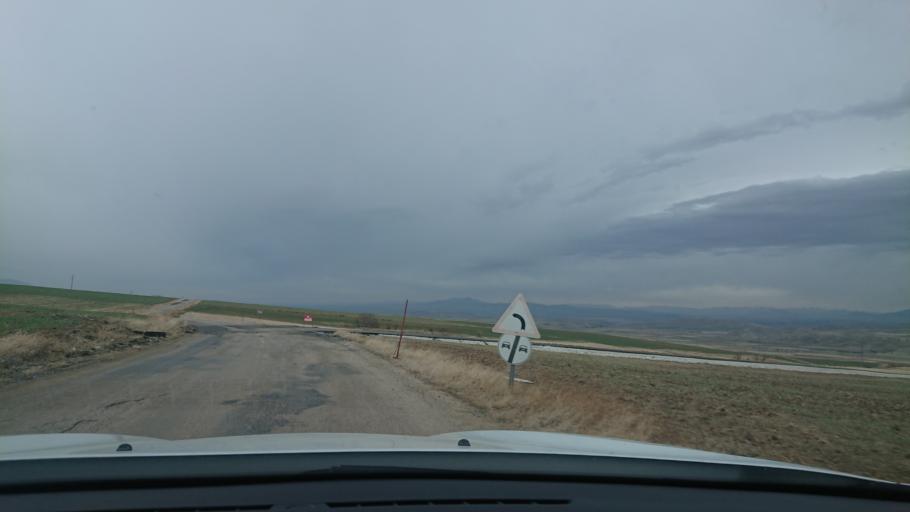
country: TR
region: Aksaray
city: Agacoren
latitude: 38.9434
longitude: 33.9112
